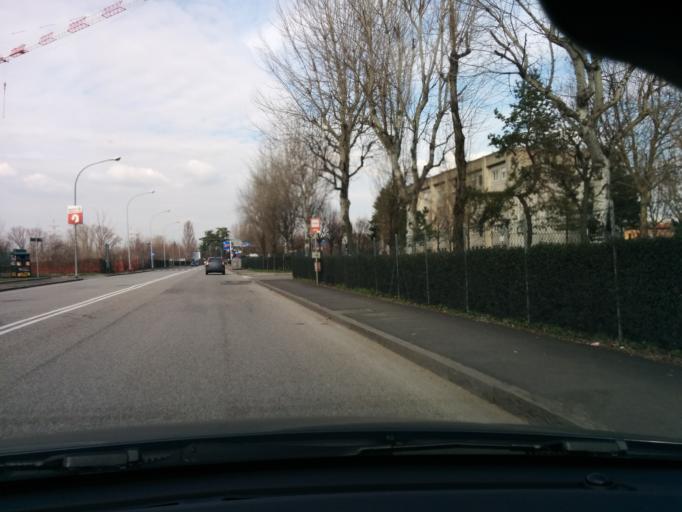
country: IT
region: Emilia-Romagna
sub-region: Provincia di Bologna
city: Bologna
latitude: 44.5236
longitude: 11.3302
